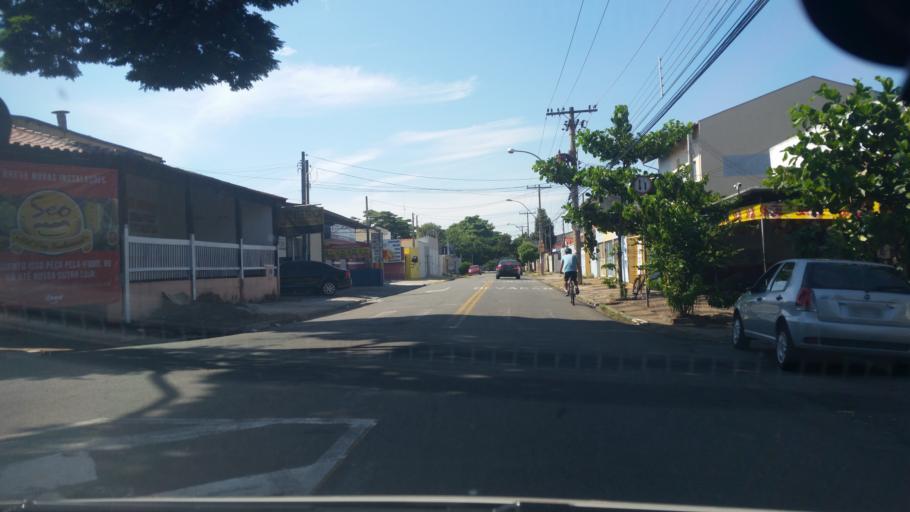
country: BR
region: Sao Paulo
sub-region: Campinas
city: Campinas
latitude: -22.8624
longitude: -47.0668
